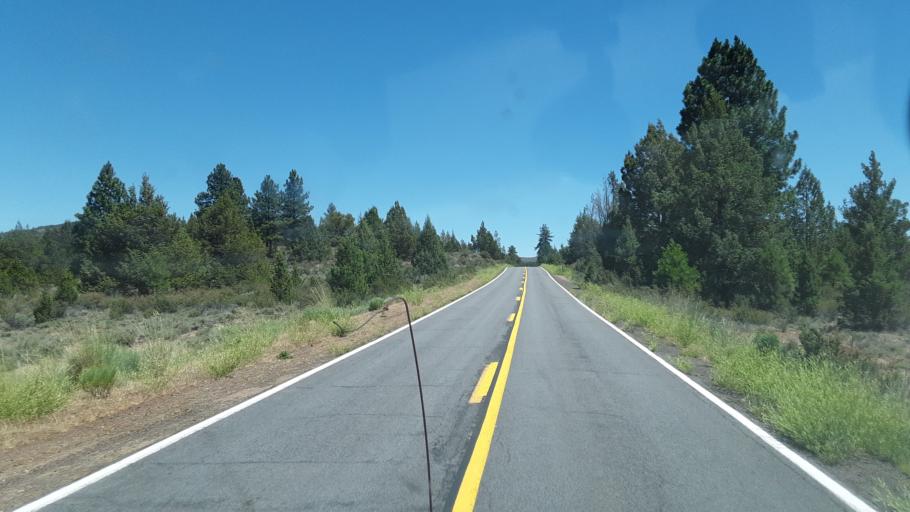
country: US
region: California
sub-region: Lassen County
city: Susanville
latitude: 40.6360
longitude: -120.6521
